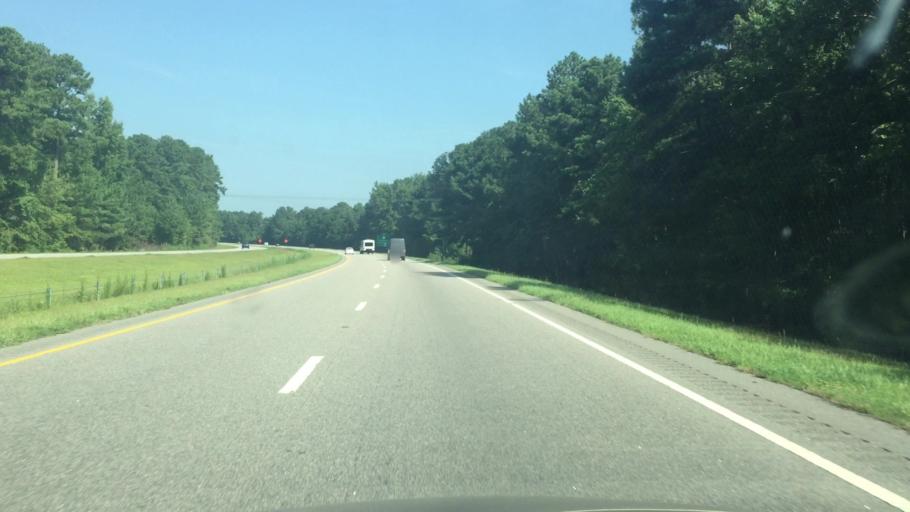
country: US
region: North Carolina
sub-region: Robeson County
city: Lumberton
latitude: 34.5659
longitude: -79.0286
